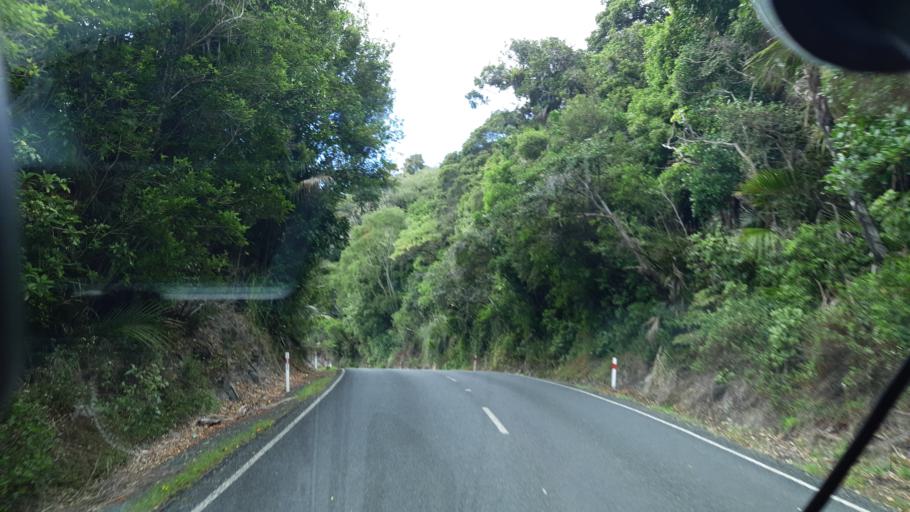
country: NZ
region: Northland
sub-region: Far North District
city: Taipa
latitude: -35.2472
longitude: 173.5305
